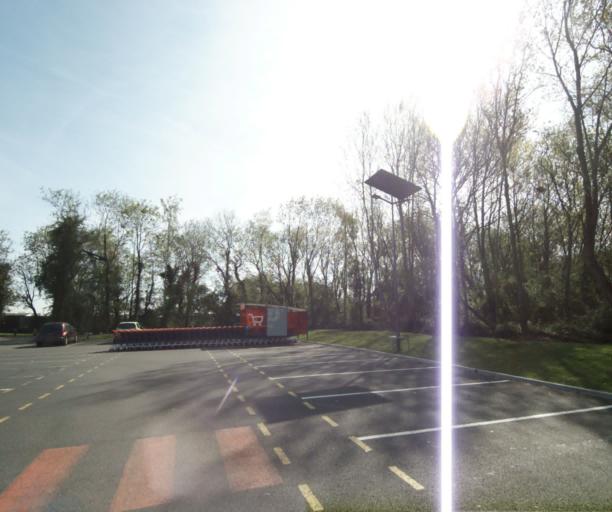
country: FR
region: Ile-de-France
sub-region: Departement de Seine-et-Marne
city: Nangis
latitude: 48.5570
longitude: 3.0255
